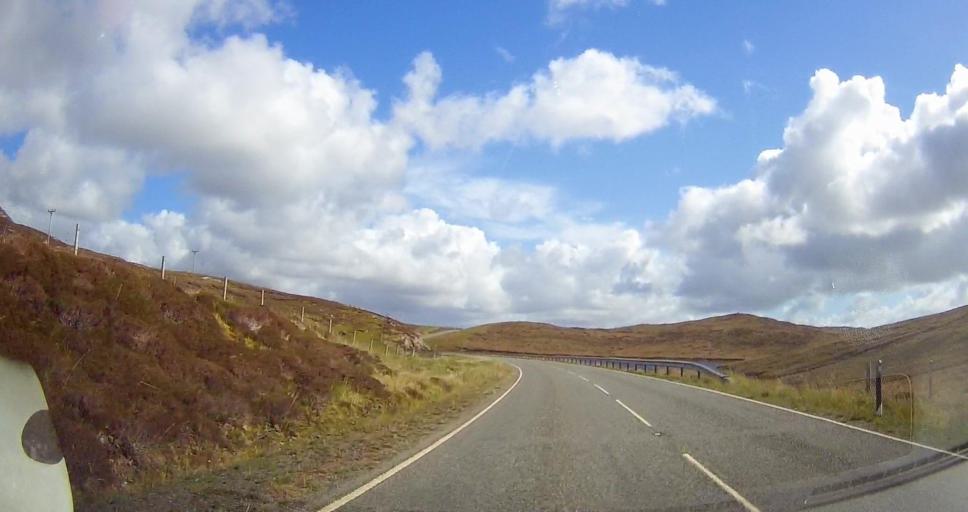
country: GB
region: Scotland
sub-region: Shetland Islands
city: Lerwick
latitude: 60.4608
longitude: -1.4037
